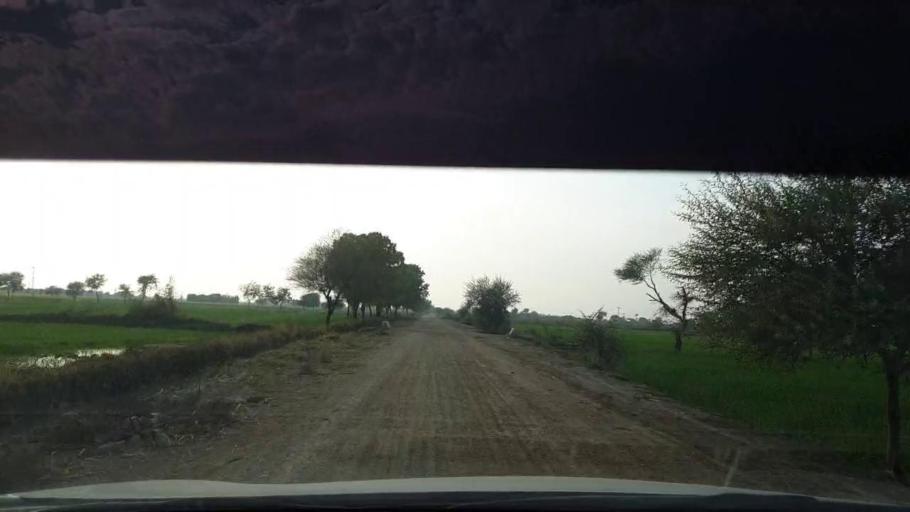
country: PK
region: Sindh
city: Berani
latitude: 25.7492
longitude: 68.9588
